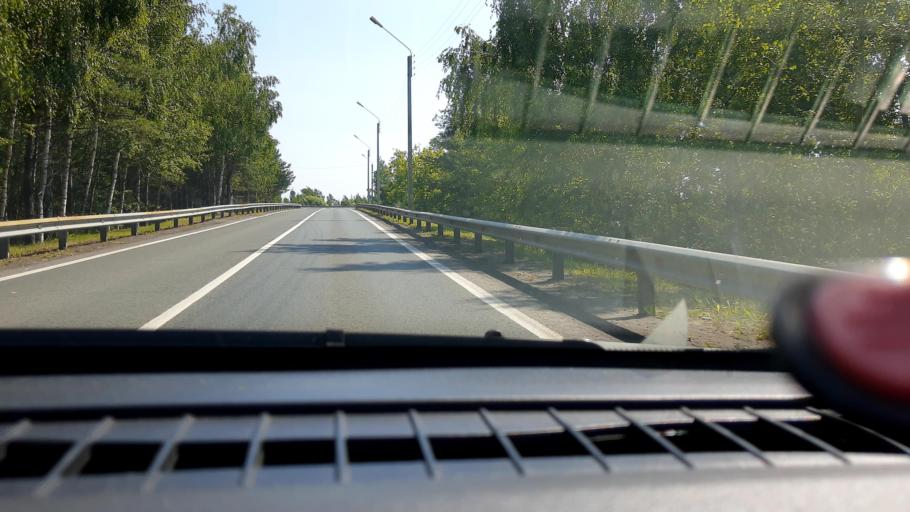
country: RU
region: Nizjnij Novgorod
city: Gorbatovka
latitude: 56.2616
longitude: 43.7039
